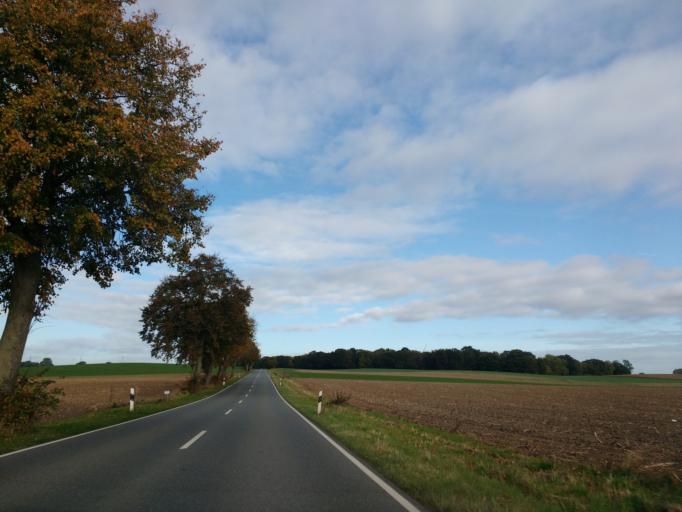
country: DE
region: Schleswig-Holstein
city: Altenkrempe
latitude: 54.1449
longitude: 10.8213
